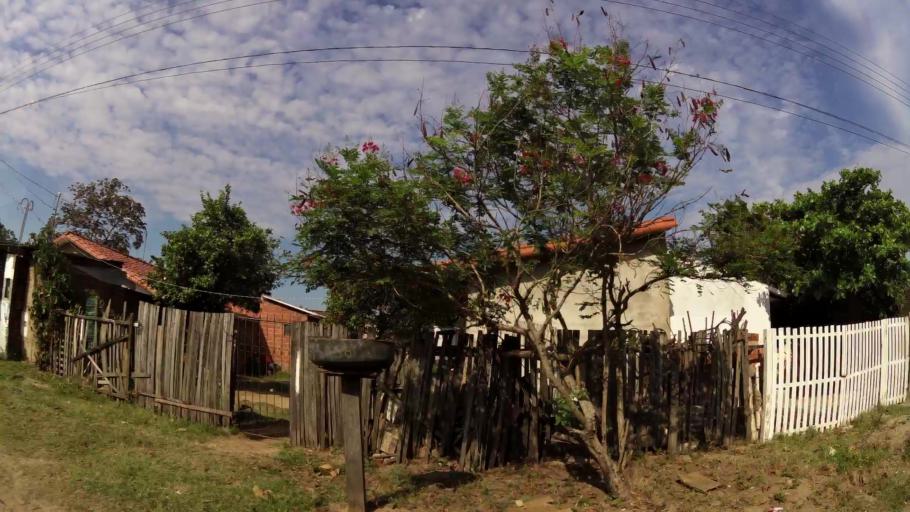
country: BO
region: Santa Cruz
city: Santa Cruz de la Sierra
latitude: -17.7333
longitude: -63.1358
